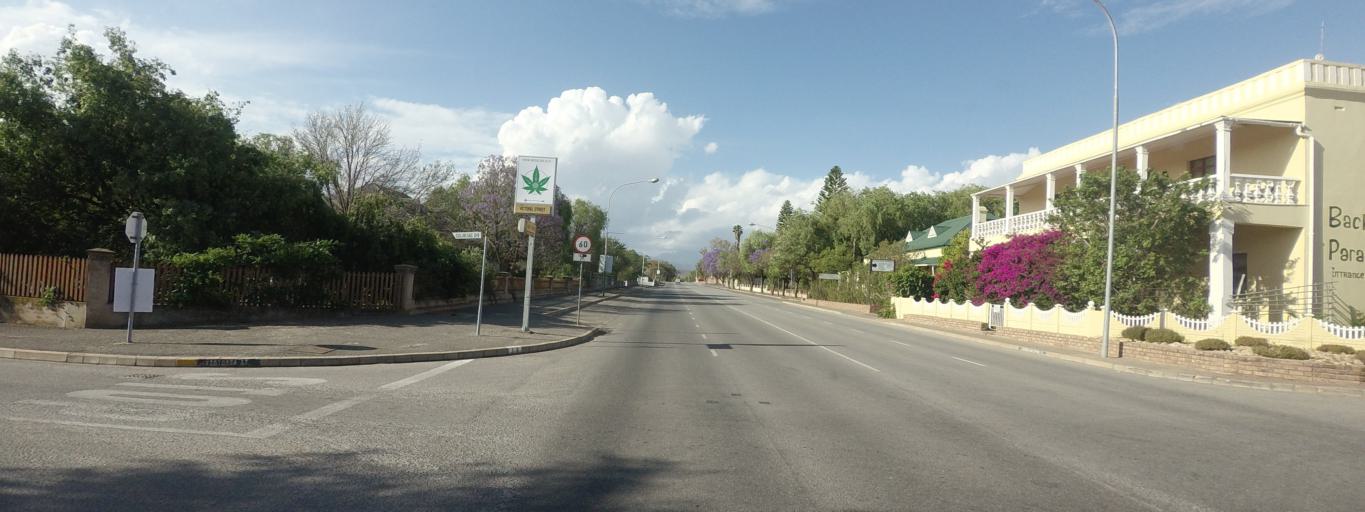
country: ZA
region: Western Cape
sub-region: Eden District Municipality
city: Oudtshoorn
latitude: -33.5802
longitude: 22.2050
